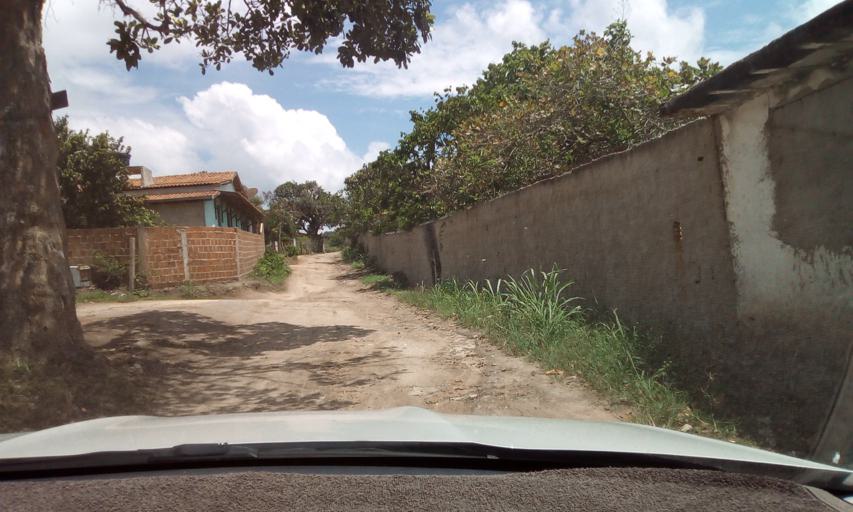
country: BR
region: Pernambuco
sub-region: Cha Grande
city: Cha Grande
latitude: -8.1956
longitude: -35.4953
